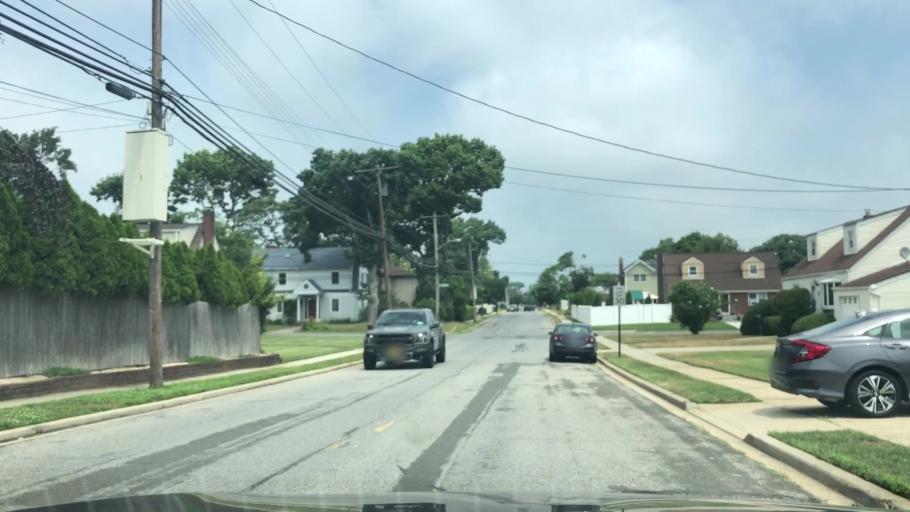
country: US
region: New York
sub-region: Nassau County
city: North Massapequa
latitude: 40.6966
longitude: -73.4677
